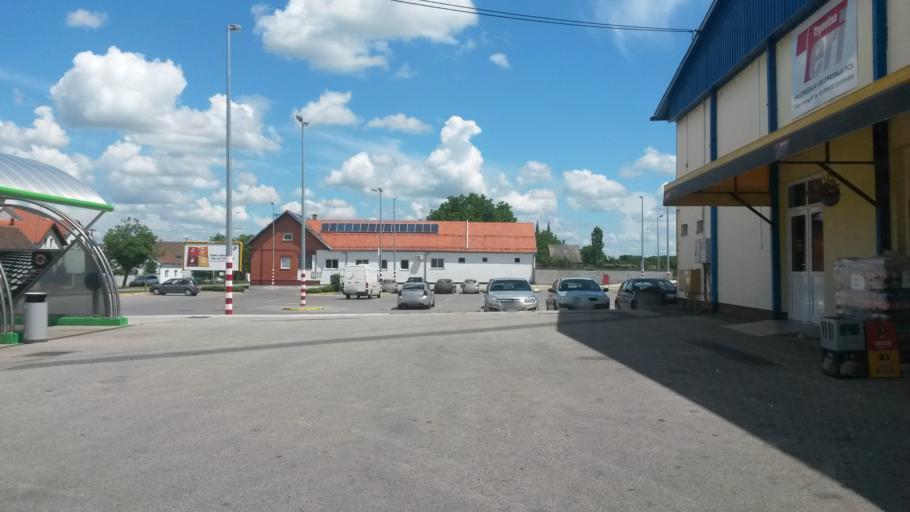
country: HR
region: Osjecko-Baranjska
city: Piskorevci
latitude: 45.3105
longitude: 18.3966
